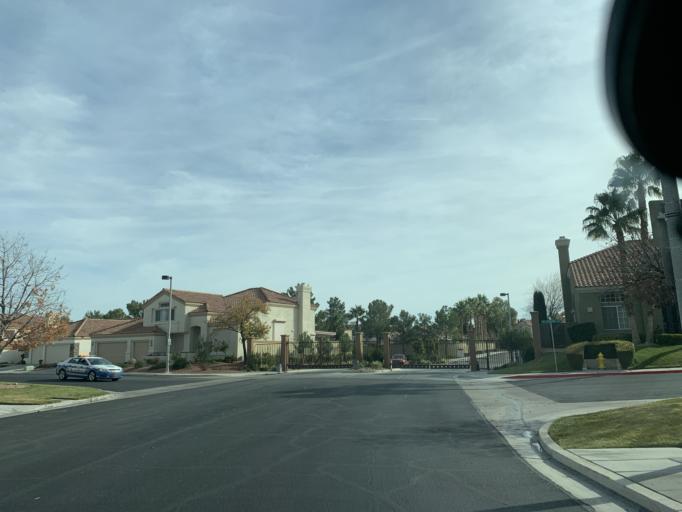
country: US
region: Nevada
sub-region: Clark County
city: Summerlin South
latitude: 36.1511
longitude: -115.3008
